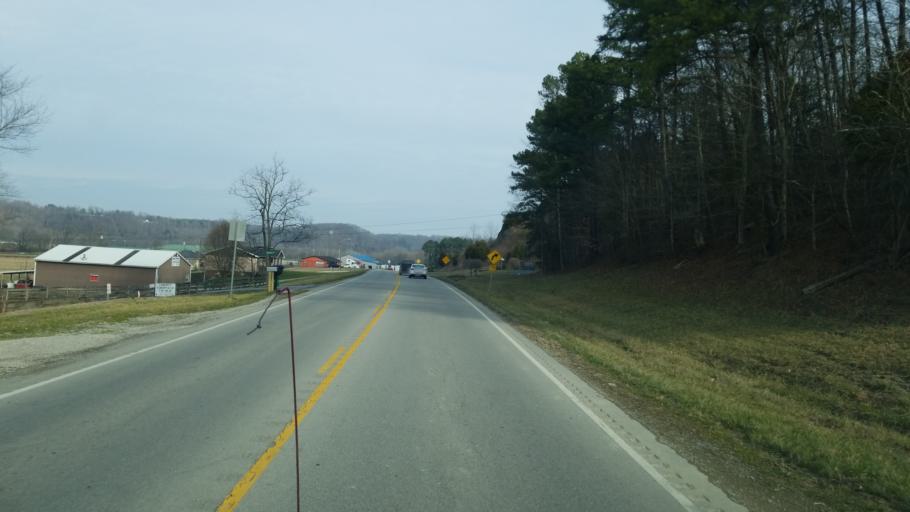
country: US
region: Kentucky
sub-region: Casey County
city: Liberty
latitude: 37.3044
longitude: -84.9458
